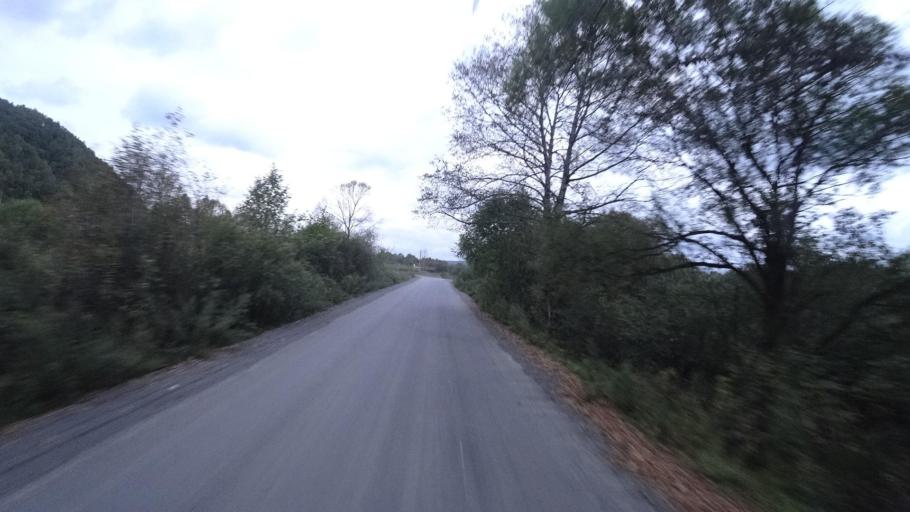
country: RU
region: Jewish Autonomous Oblast
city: Izvestkovyy
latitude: 48.9926
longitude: 131.5405
